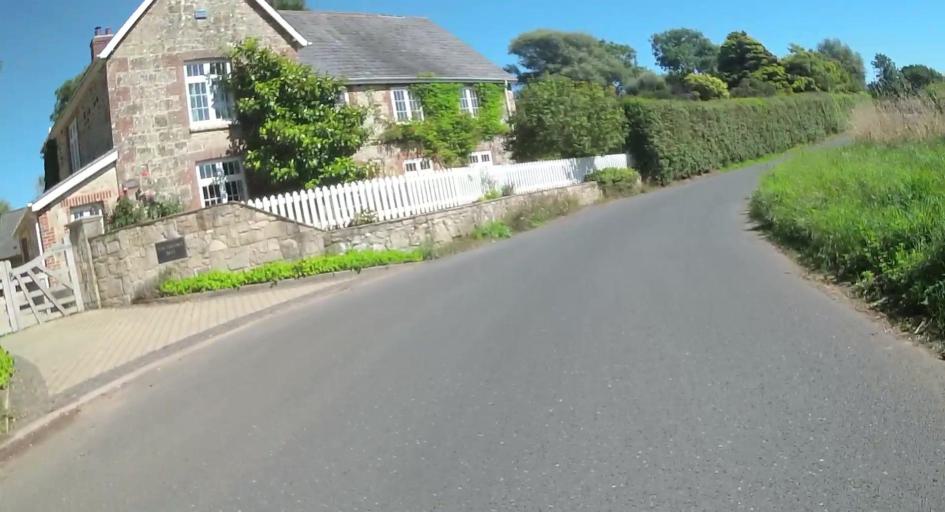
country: GB
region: England
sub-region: Isle of Wight
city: Niton
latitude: 50.6079
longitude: -1.2731
